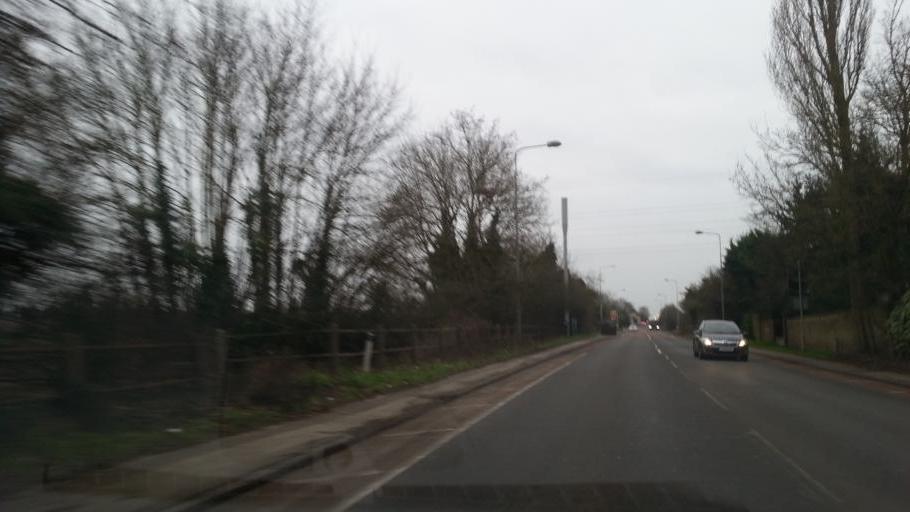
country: GB
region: England
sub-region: Central Bedfordshire
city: Hockliffe
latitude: 51.9272
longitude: -0.5804
